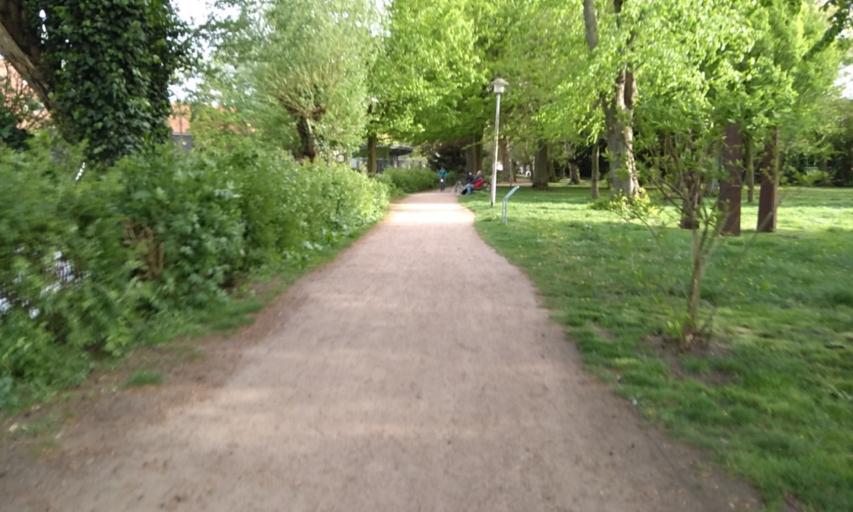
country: DE
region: Lower Saxony
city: Buxtehude
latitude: 53.4762
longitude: 9.6963
